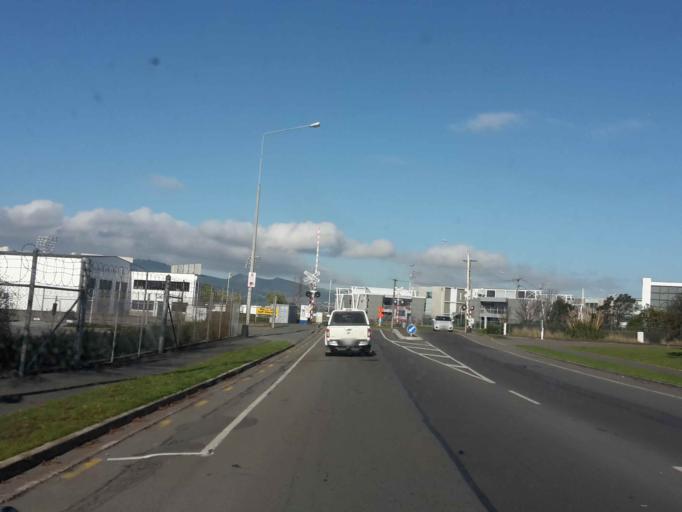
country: NZ
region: Canterbury
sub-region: Christchurch City
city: Christchurch
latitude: -43.5402
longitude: 172.5970
